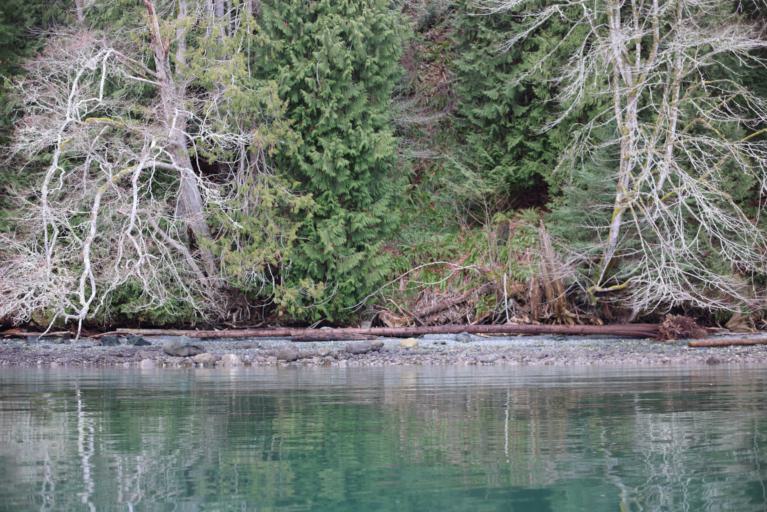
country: CA
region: British Columbia
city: Duncan
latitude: 48.7227
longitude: -123.5651
